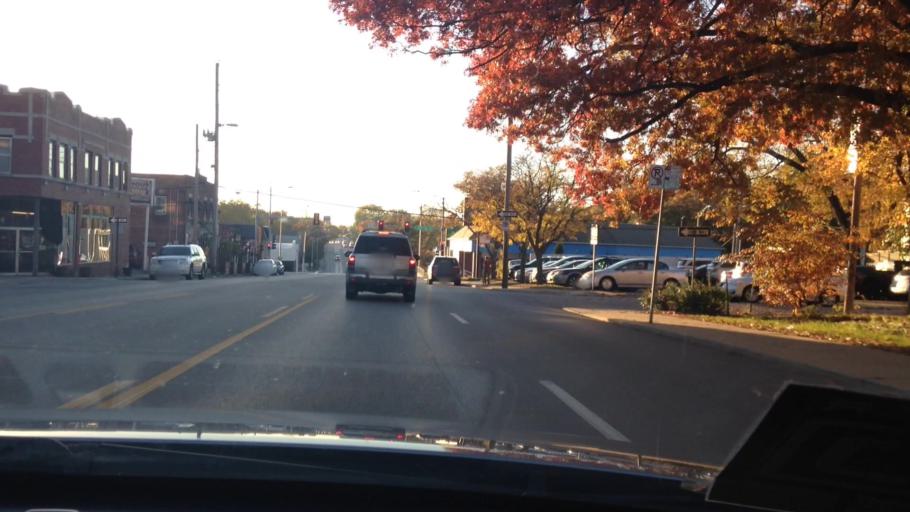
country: US
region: Kansas
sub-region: Johnson County
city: Westwood
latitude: 39.0502
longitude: -94.6060
